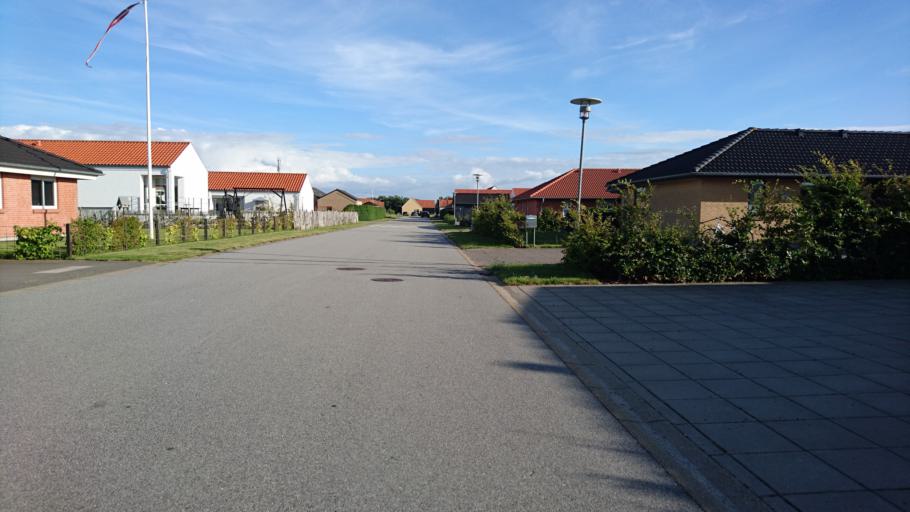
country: DK
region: North Denmark
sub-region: Frederikshavn Kommune
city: Skagen
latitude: 57.7337
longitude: 10.5911
